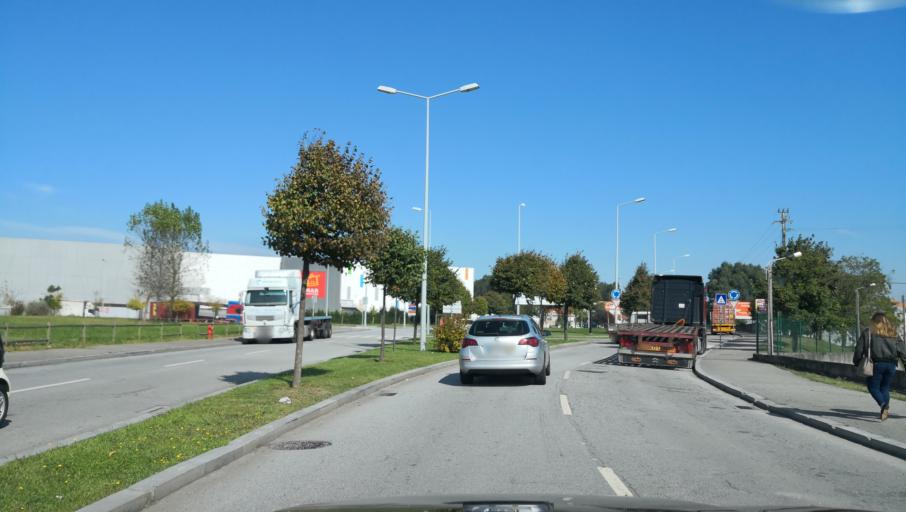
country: PT
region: Porto
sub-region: Matosinhos
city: Leca da Palmeira
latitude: 41.2056
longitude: -8.6870
